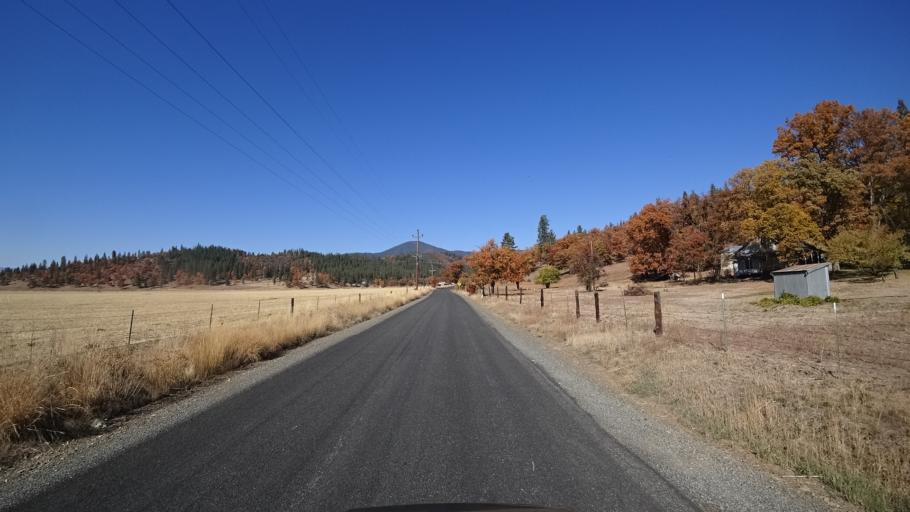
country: US
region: California
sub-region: Siskiyou County
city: Yreka
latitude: 41.6295
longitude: -122.8731
